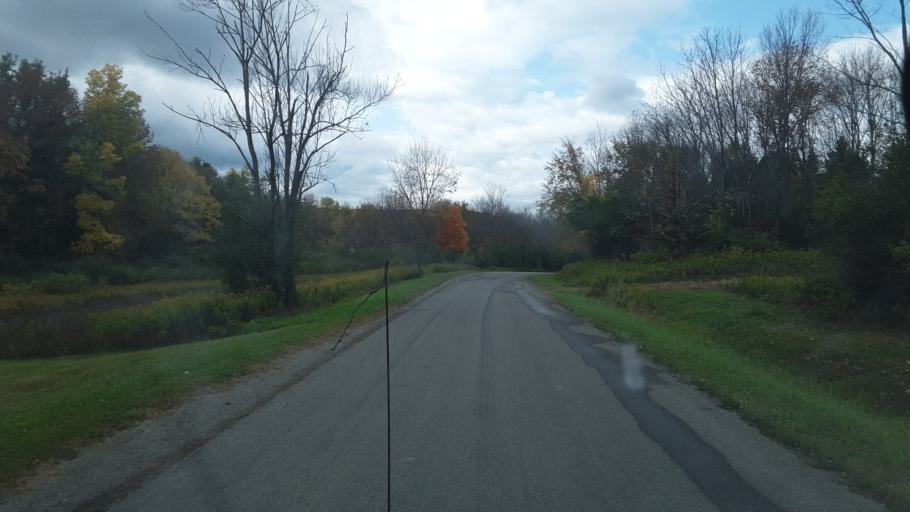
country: US
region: New York
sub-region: Allegany County
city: Alfred
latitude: 42.3645
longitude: -77.8331
